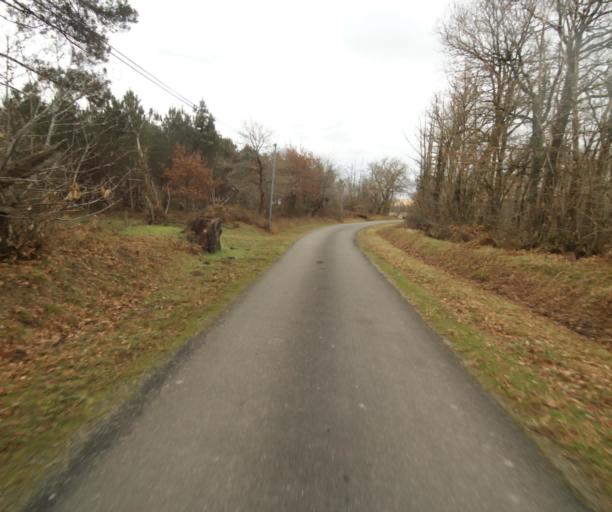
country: FR
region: Aquitaine
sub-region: Departement des Landes
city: Gabarret
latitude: 44.0165
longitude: -0.0597
